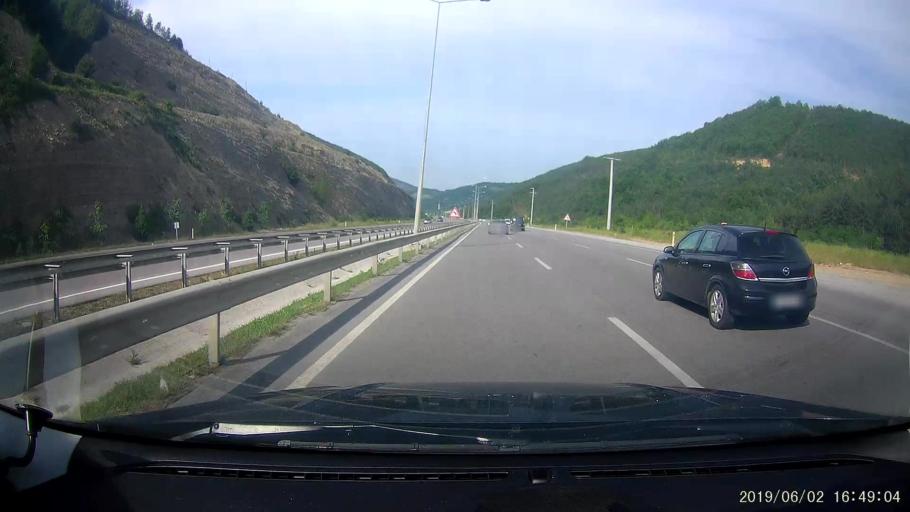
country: TR
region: Samsun
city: Taflan
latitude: 41.2327
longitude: 36.1532
